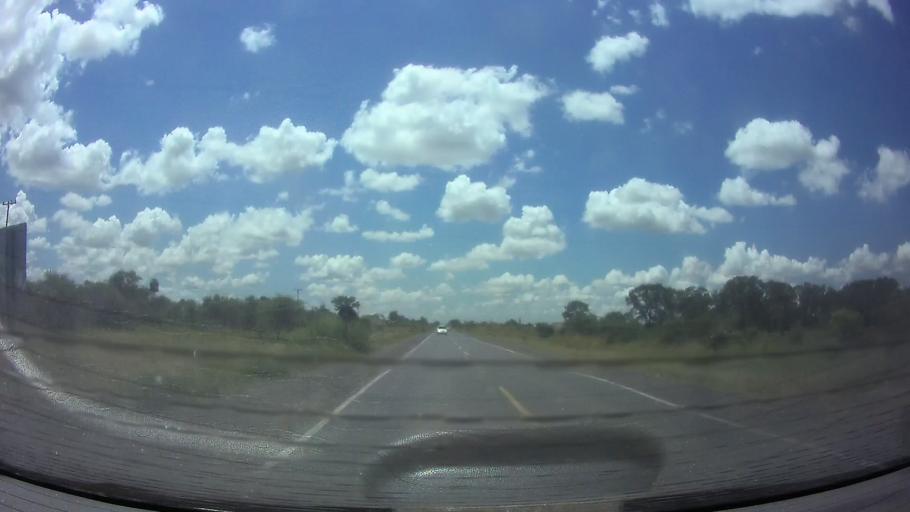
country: PY
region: Presidente Hayes
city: Nanawa
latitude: -25.2228
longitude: -57.6805
